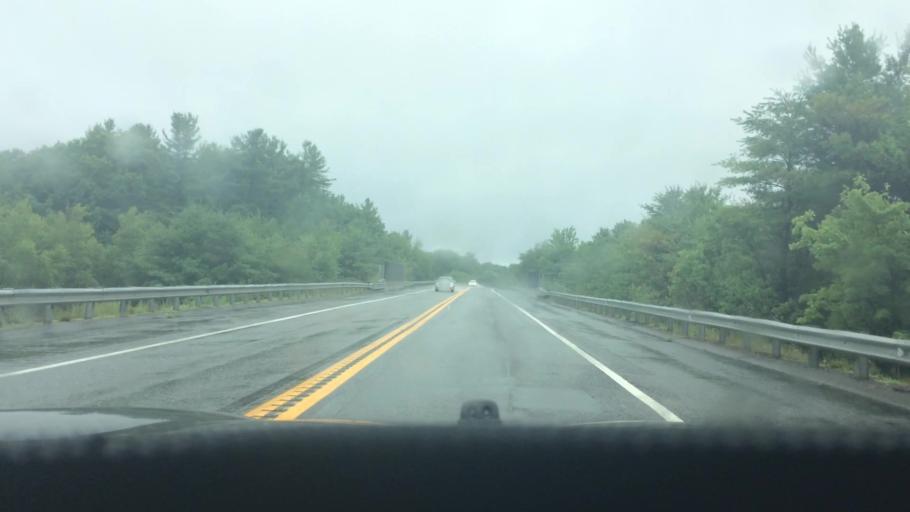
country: US
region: Massachusetts
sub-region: Worcester County
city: South Ashburnham
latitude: 42.5738
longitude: -71.9476
